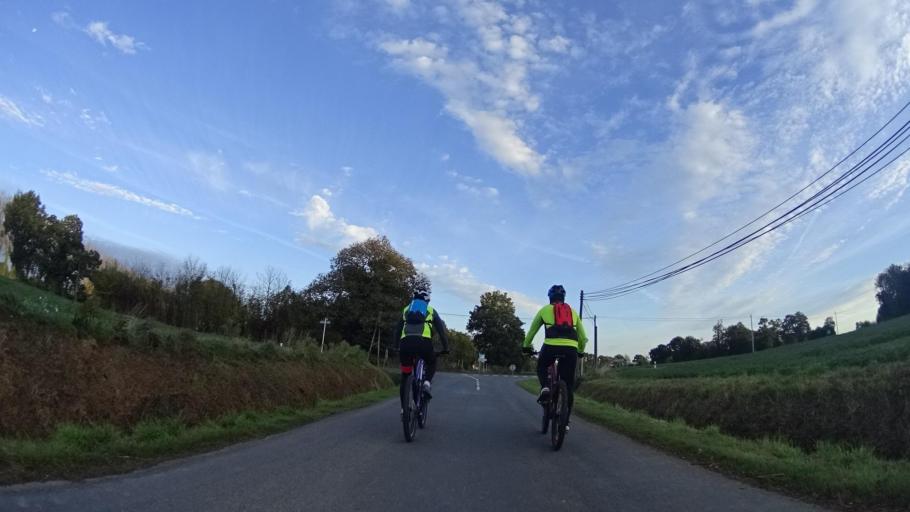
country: FR
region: Brittany
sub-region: Departement des Cotes-d'Armor
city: Evran
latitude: 48.3441
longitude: -1.9397
